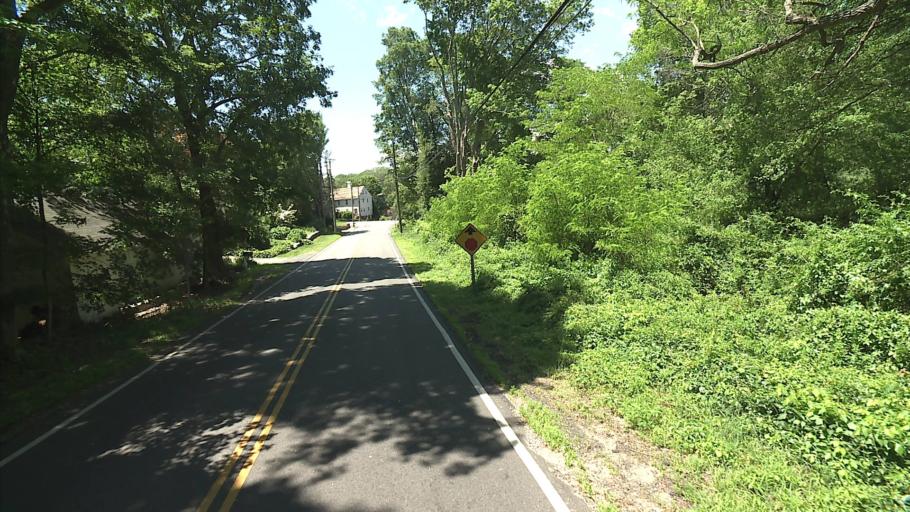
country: US
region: Connecticut
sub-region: New London County
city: Old Mystic
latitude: 41.3884
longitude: -71.9563
